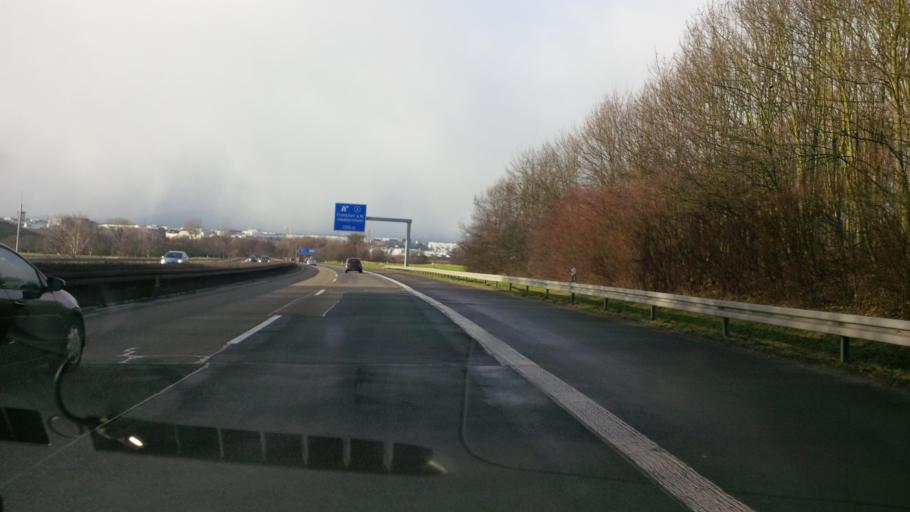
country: DE
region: Hesse
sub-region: Regierungsbezirk Darmstadt
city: Frankfurt am Main
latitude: 50.1692
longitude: 8.6596
